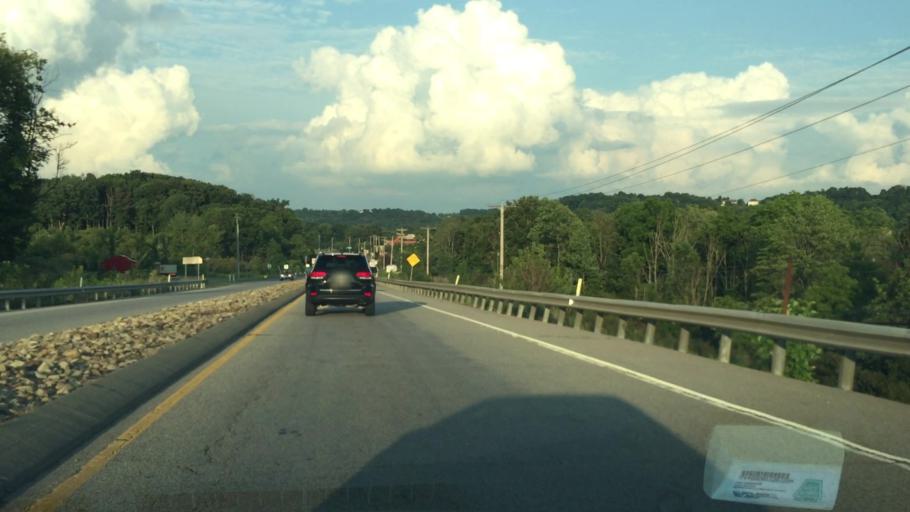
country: US
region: Pennsylvania
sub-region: Butler County
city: Seven Fields
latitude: 40.6854
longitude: -80.0723
